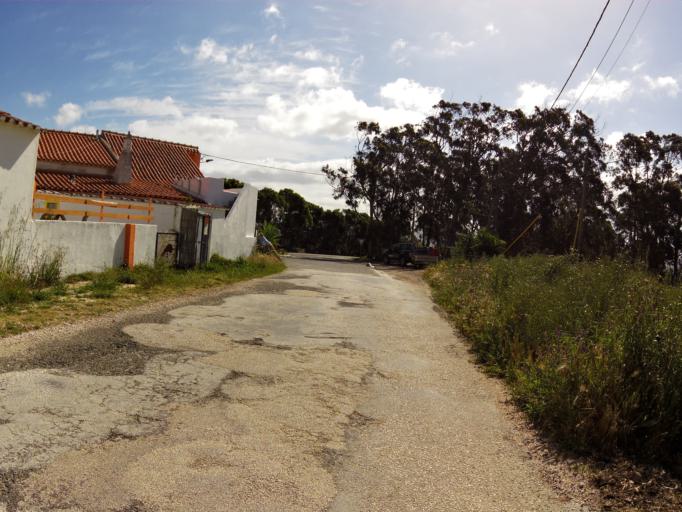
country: PT
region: Faro
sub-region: Aljezur
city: Aljezur
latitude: 37.3410
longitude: -8.8010
